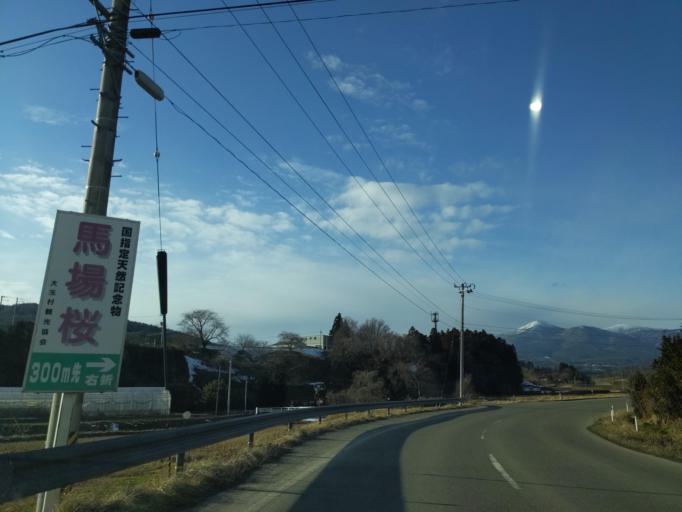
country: JP
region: Fukushima
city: Motomiya
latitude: 37.5282
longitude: 140.3632
